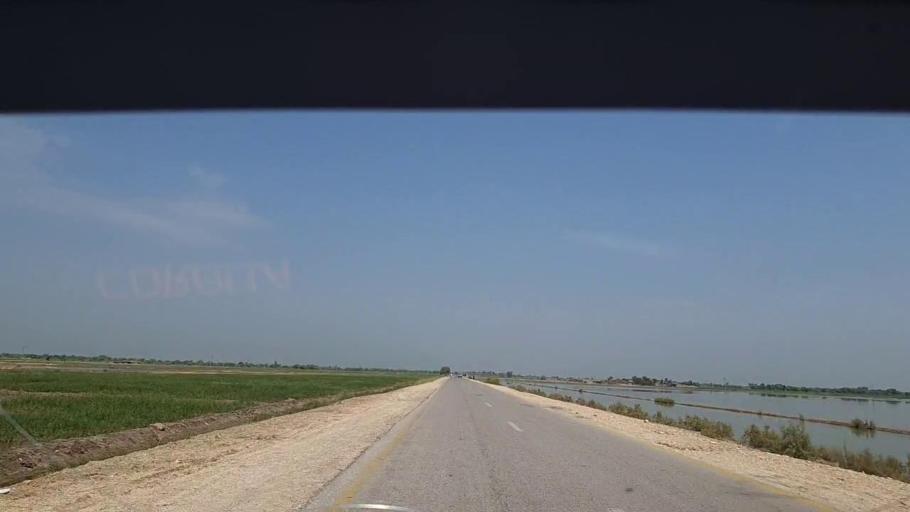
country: PK
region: Sindh
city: Rustam jo Goth
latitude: 28.0909
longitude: 68.7994
